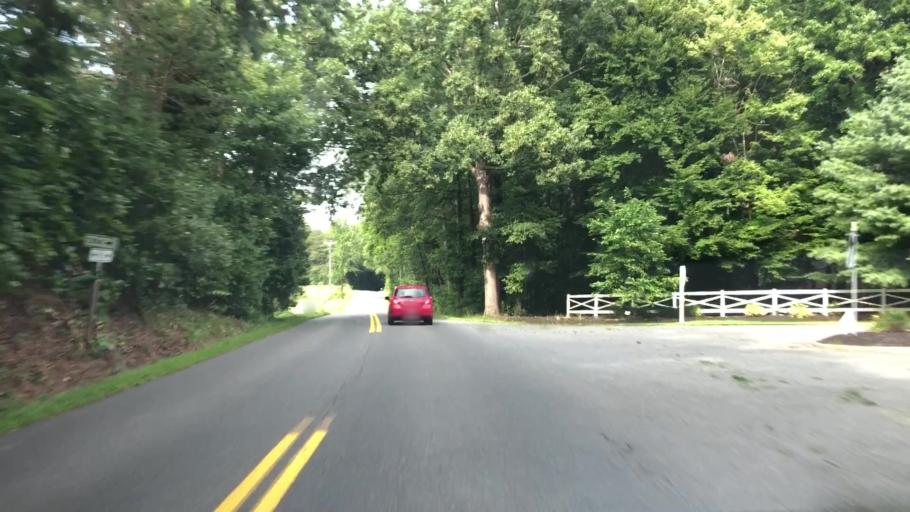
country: US
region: Virginia
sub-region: Stafford County
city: Falmouth
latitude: 38.4116
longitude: -77.5042
